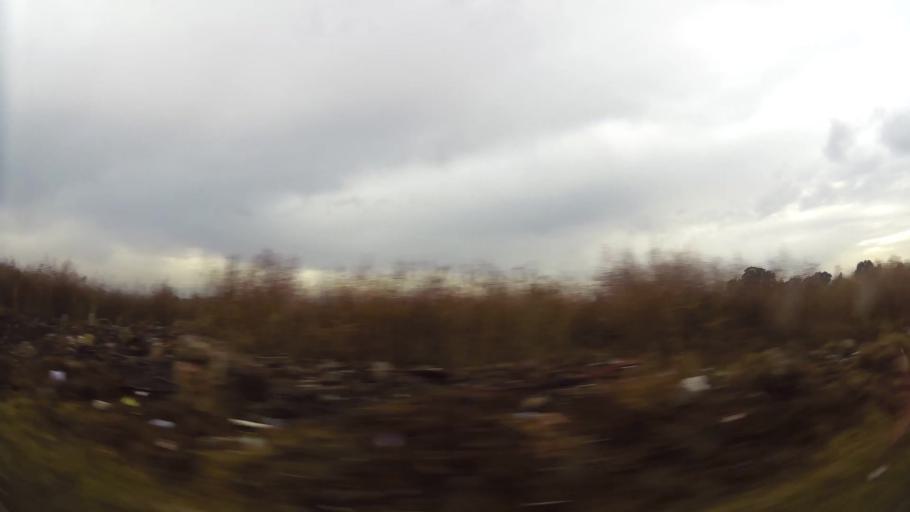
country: ZA
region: Gauteng
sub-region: Ekurhuleni Metropolitan Municipality
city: Germiston
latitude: -26.3376
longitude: 28.1936
